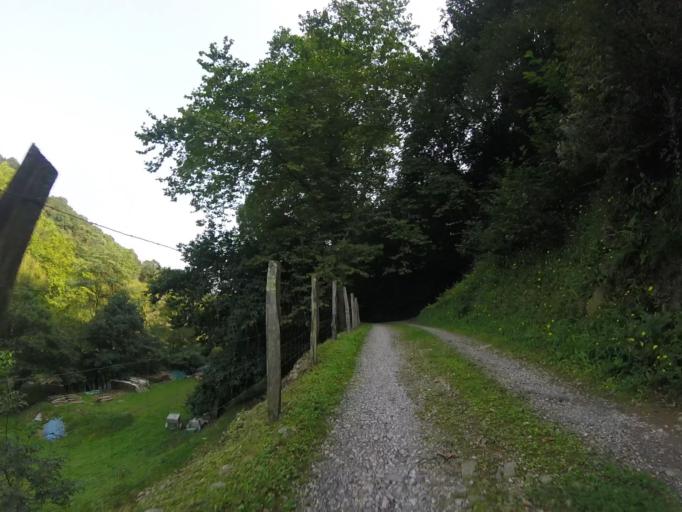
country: ES
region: Navarre
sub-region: Provincia de Navarra
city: Arano
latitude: 43.2251
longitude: -1.9321
